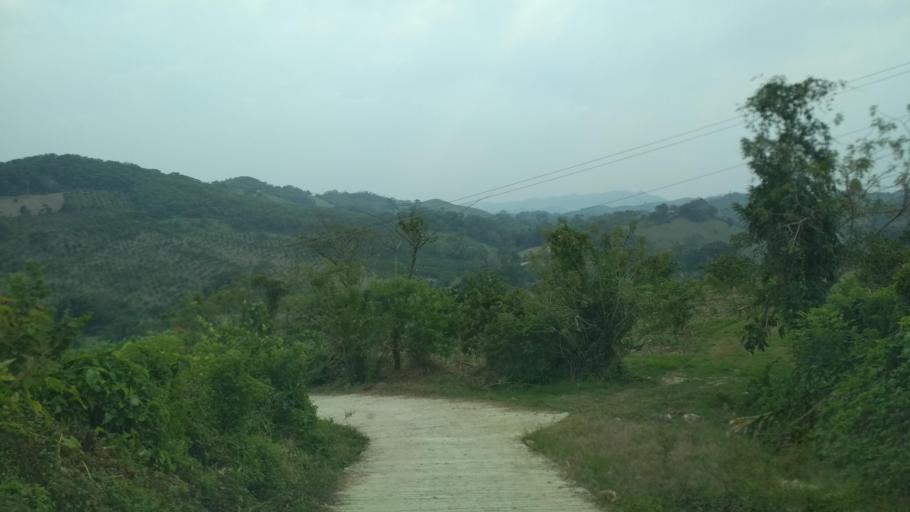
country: MM
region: Kayah
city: Loikaw
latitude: 20.2028
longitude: 97.3035
